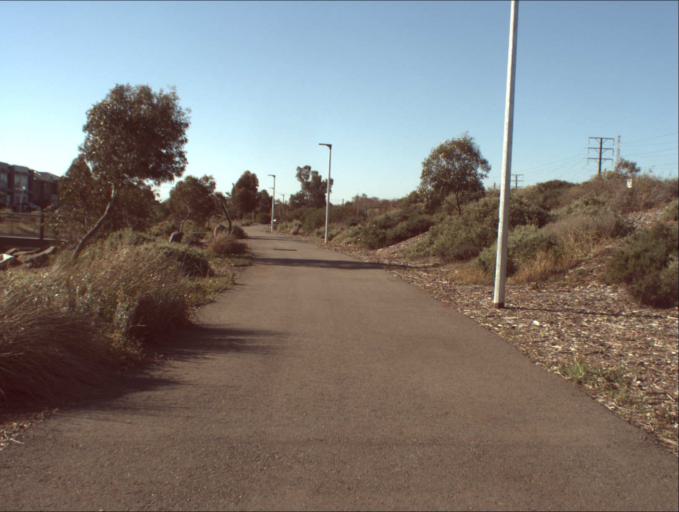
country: AU
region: South Australia
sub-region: Port Adelaide Enfield
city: Birkenhead
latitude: -34.8132
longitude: 138.5074
